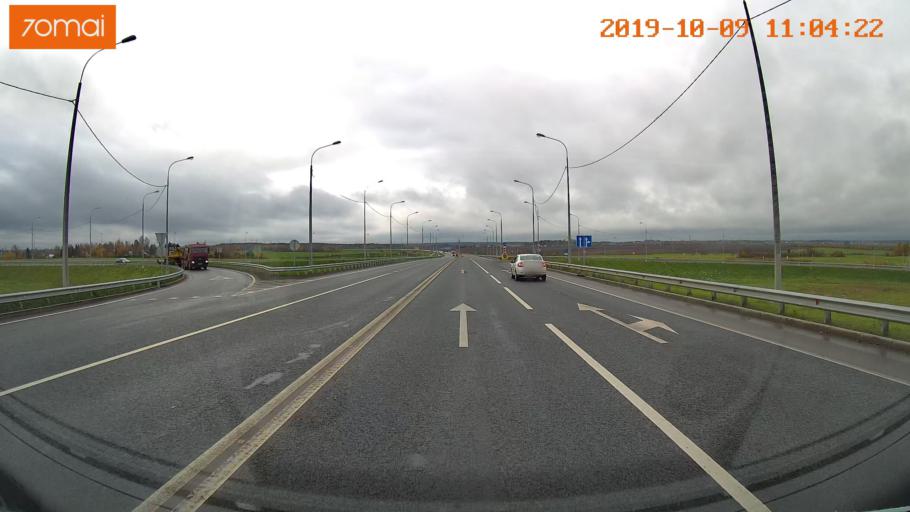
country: RU
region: Vologda
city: Vologda
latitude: 59.2128
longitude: 39.7681
